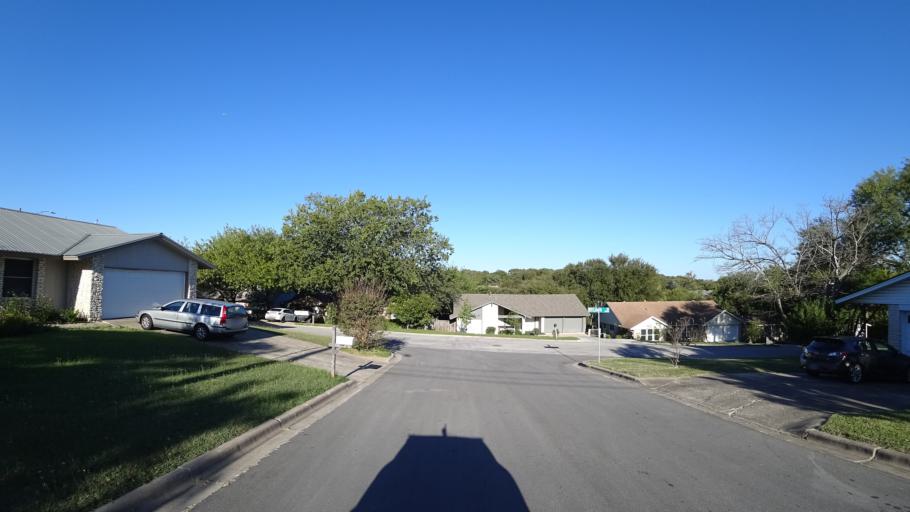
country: US
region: Texas
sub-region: Travis County
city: Austin
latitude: 30.3064
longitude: -97.6725
